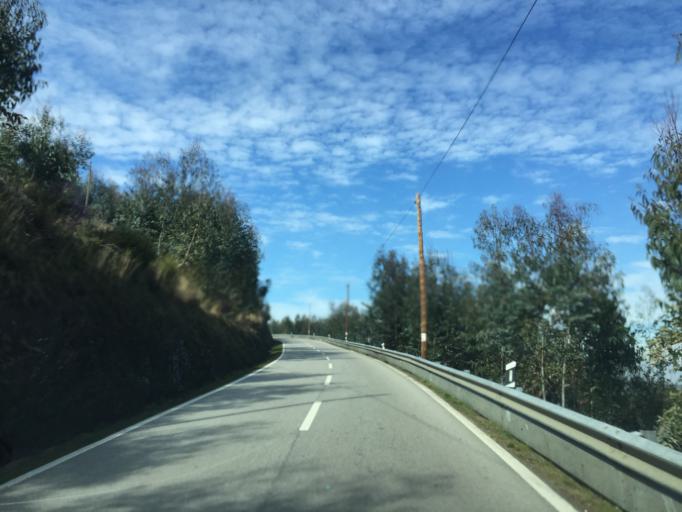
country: PT
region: Aveiro
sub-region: Arouca
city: Arouca
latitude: 40.9595
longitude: -8.2030
